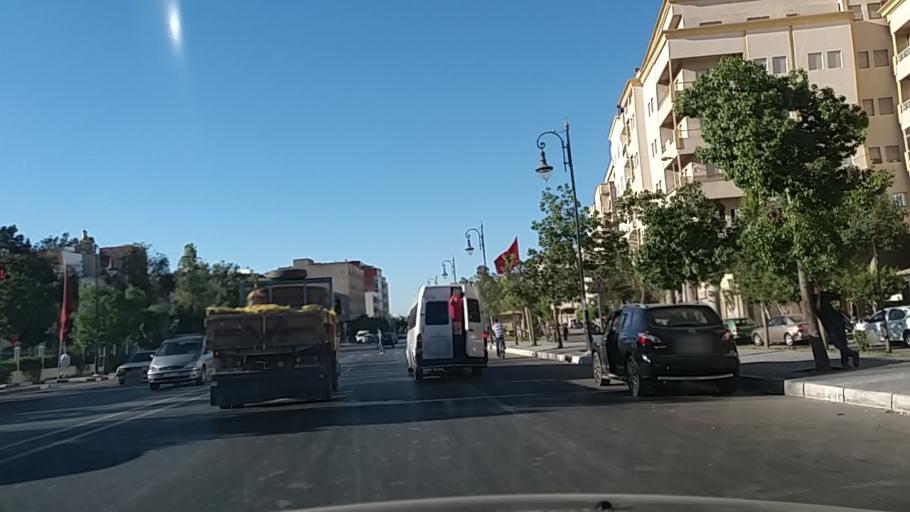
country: MA
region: Tanger-Tetouan
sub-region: Tanger-Assilah
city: Tangier
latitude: 35.7439
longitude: -5.7991
